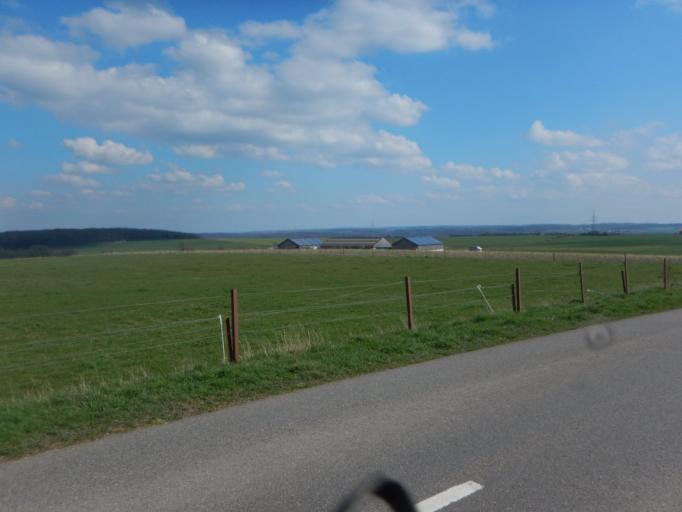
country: LU
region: Diekirch
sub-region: Canton de Diekirch
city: Medernach
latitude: 49.8081
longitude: 6.2548
